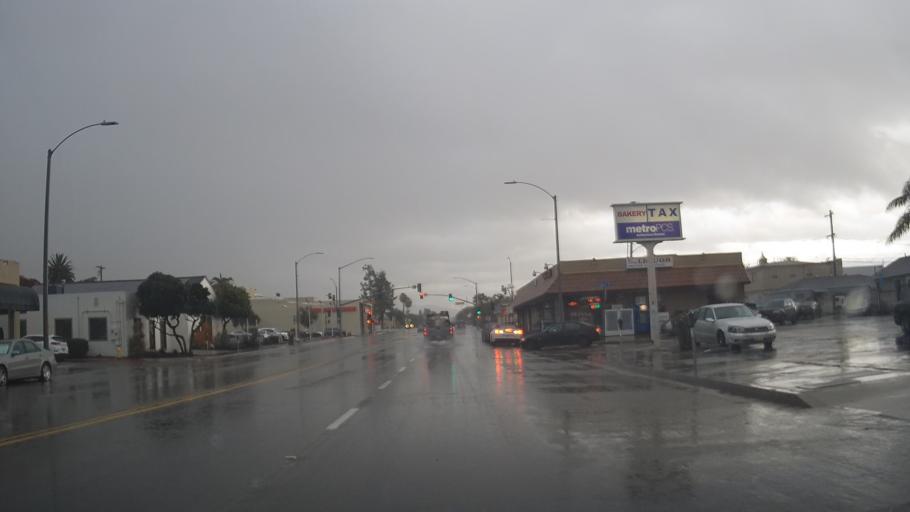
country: US
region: California
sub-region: San Diego County
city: Chula Vista
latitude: 32.6443
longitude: -117.0824
